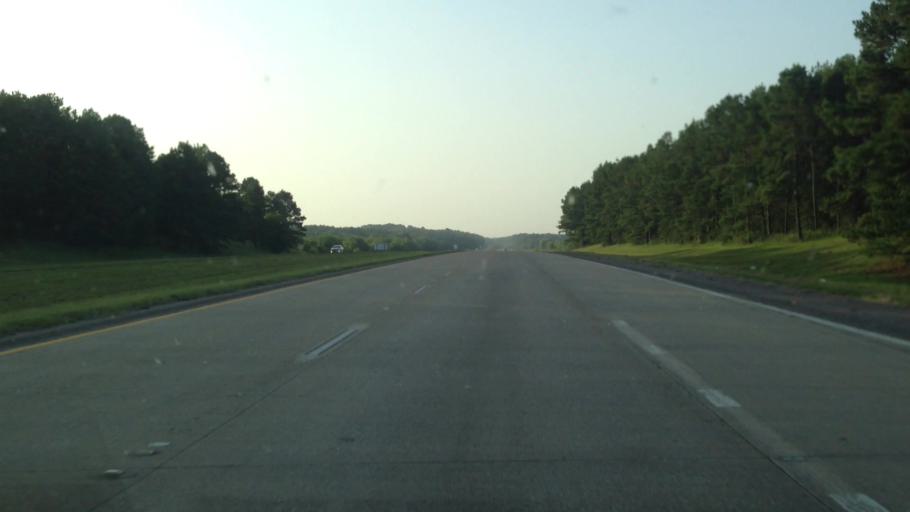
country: US
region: Louisiana
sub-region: Grant Parish
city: Colfax
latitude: 31.4903
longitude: -92.8561
